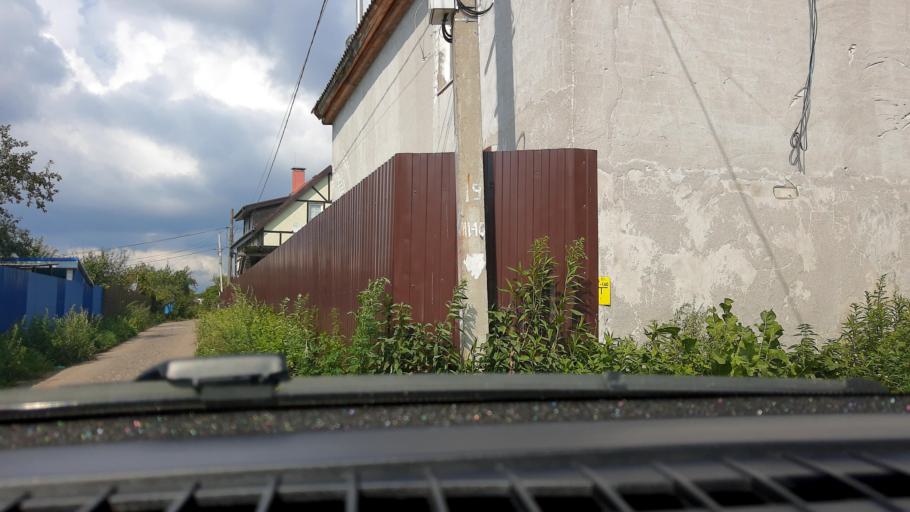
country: RU
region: Nizjnij Novgorod
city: Afonino
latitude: 56.3033
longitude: 44.0571
